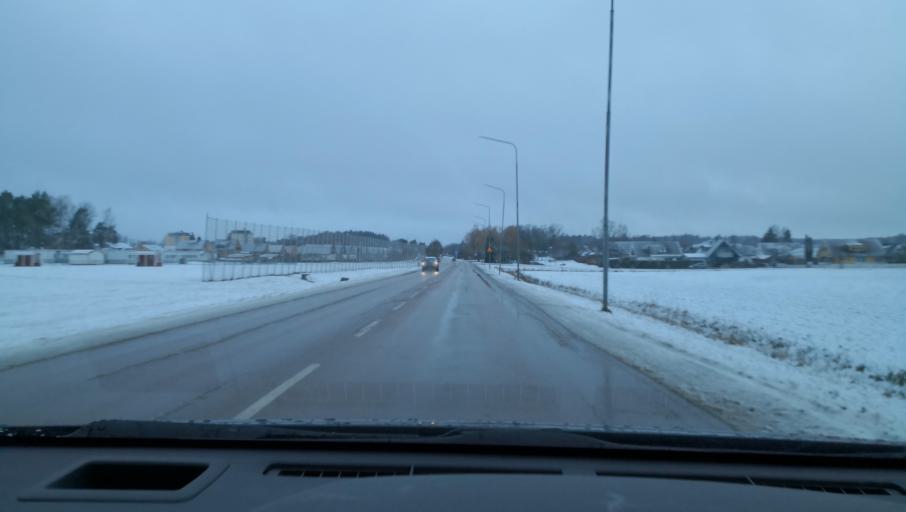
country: SE
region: Vaestmanland
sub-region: Kopings Kommun
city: Koping
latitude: 59.5153
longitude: 16.0141
